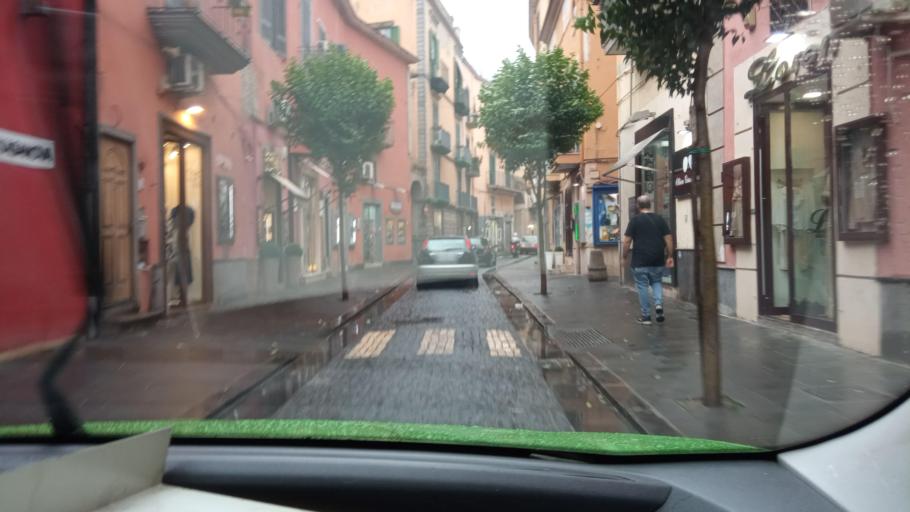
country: IT
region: Campania
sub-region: Provincia di Napoli
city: Pozzuoli
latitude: 40.8235
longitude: 14.1217
